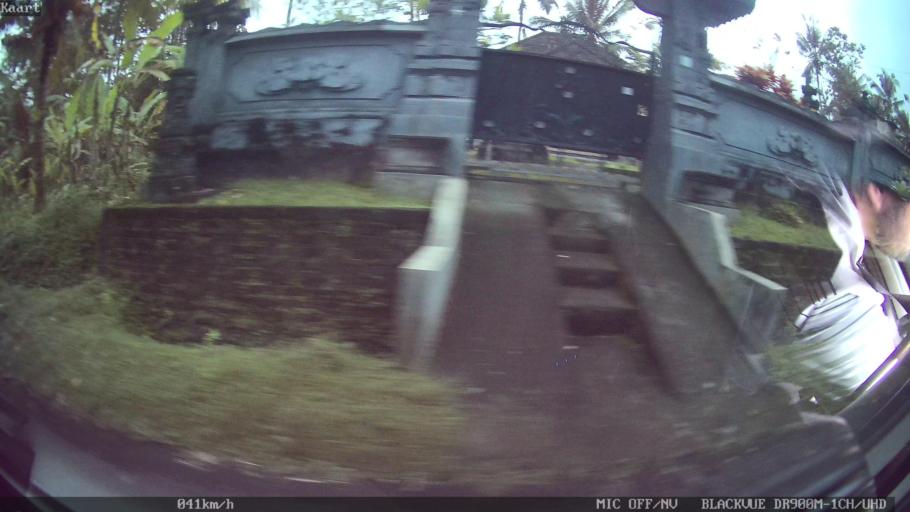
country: ID
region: Bali
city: Badung
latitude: -8.4310
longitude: 115.2260
